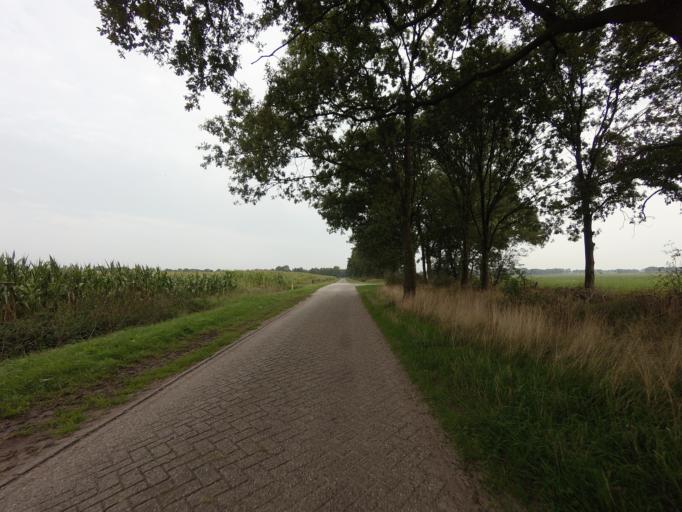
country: NL
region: Drenthe
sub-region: Gemeente Westerveld
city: Dwingeloo
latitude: 52.8558
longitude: 6.4111
